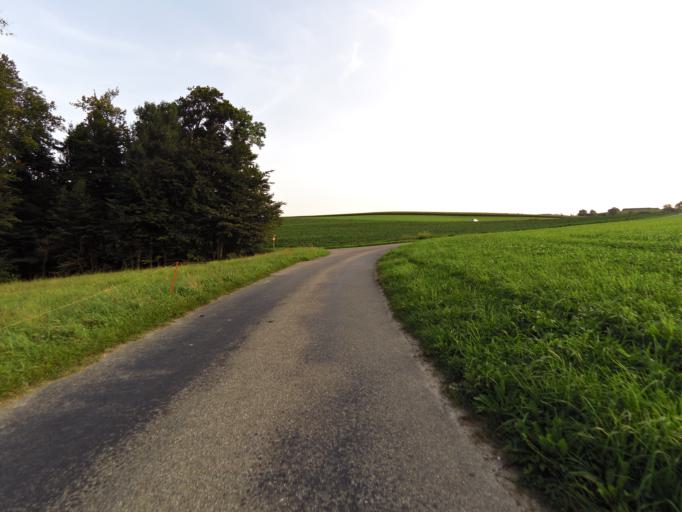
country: CH
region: Thurgau
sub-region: Frauenfeld District
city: Frauenfeld
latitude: 47.5303
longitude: 8.8851
